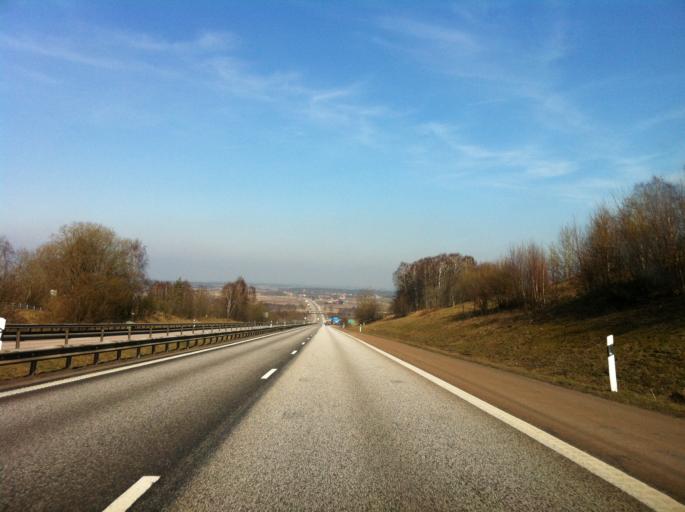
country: SE
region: Skane
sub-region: Bastads Kommun
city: Bastad
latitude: 56.4135
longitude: 12.9472
